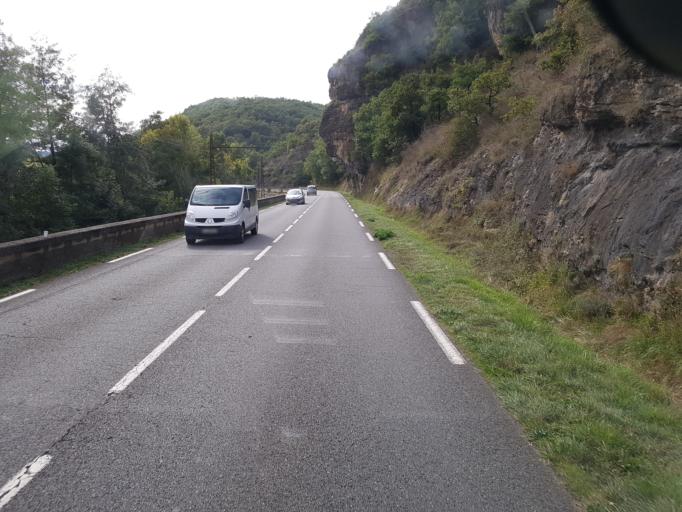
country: FR
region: Midi-Pyrenees
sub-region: Departement de l'Aveyron
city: Saint-Georges-de-Luzencon
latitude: 44.0575
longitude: 2.9811
